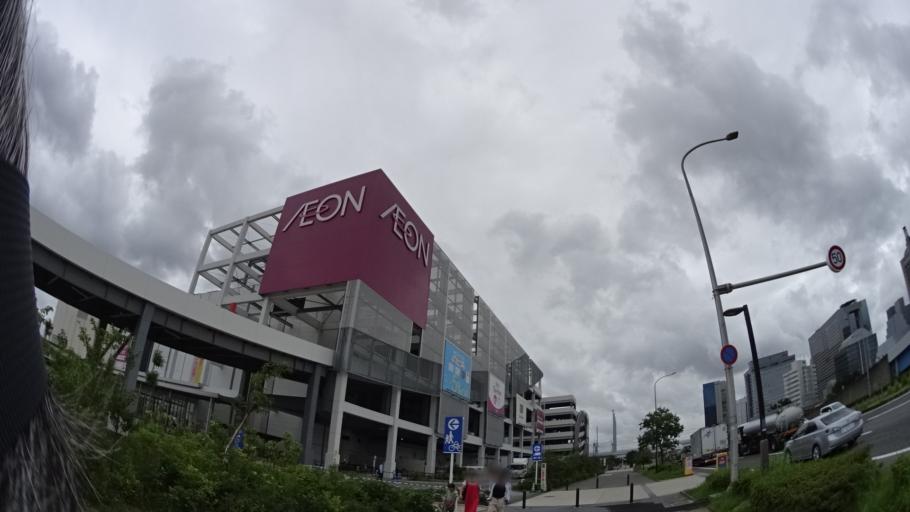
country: JP
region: Chiba
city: Funabashi
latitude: 35.6510
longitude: 140.0327
